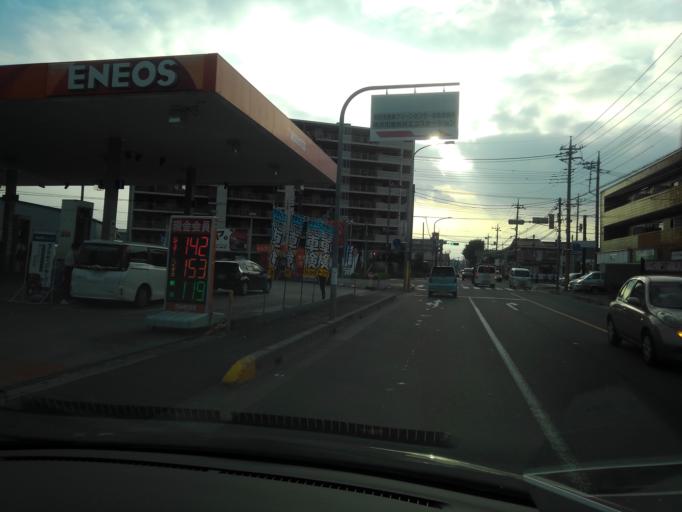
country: JP
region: Saitama
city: Tokorozawa
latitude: 35.7922
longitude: 139.5070
